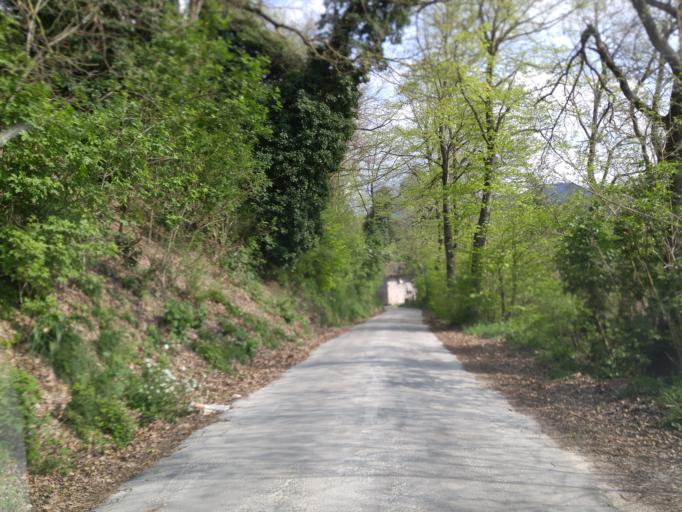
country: IT
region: The Marches
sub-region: Provincia di Pesaro e Urbino
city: Acqualagna
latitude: 43.6446
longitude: 12.6895
